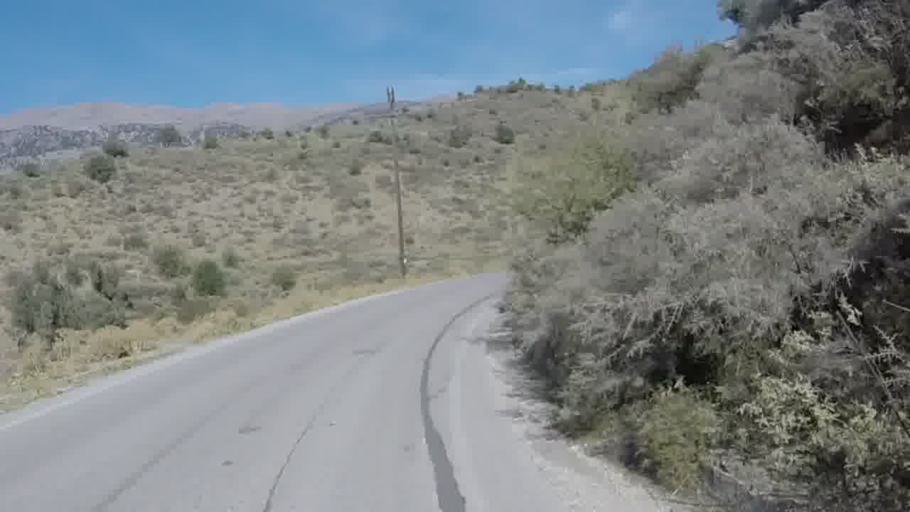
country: GR
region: Crete
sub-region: Nomos Rethymnis
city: Agia Galini
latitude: 35.1773
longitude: 24.7381
